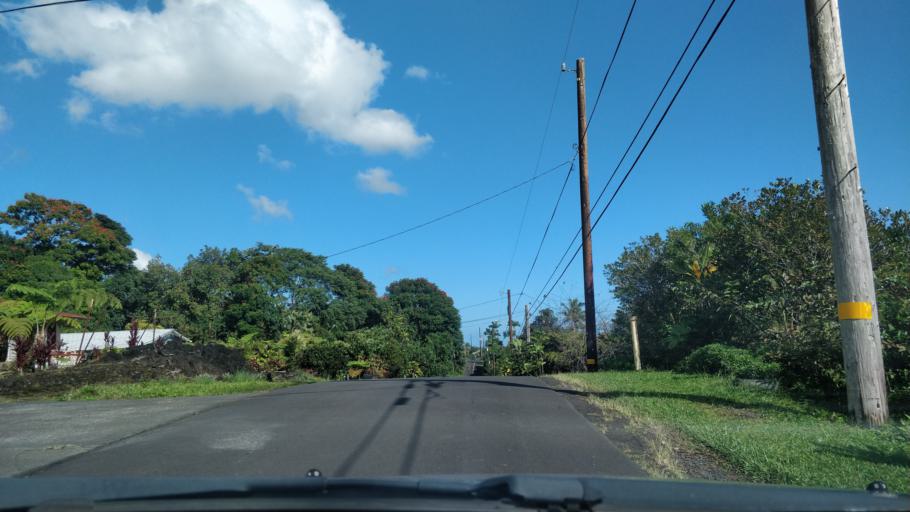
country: US
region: Hawaii
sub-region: Hawaii County
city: Hilo
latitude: 19.6616
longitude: -155.0993
